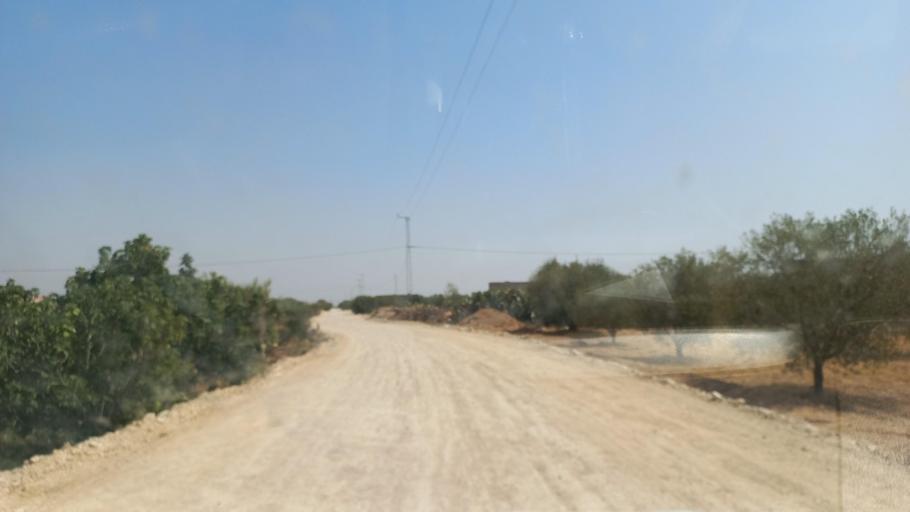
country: TN
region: Al Qasrayn
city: Kasserine
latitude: 35.2603
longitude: 9.0107
